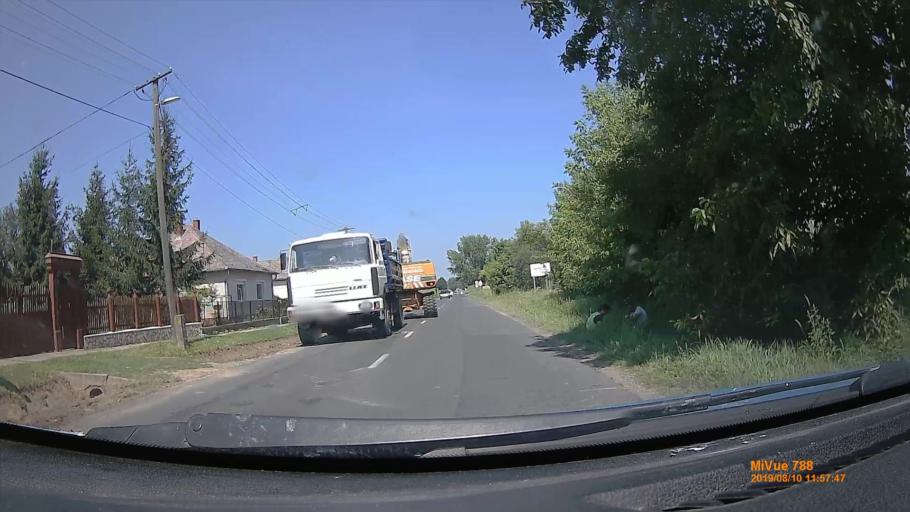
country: HU
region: Somogy
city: Somogyvar
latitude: 46.5257
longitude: 17.6649
